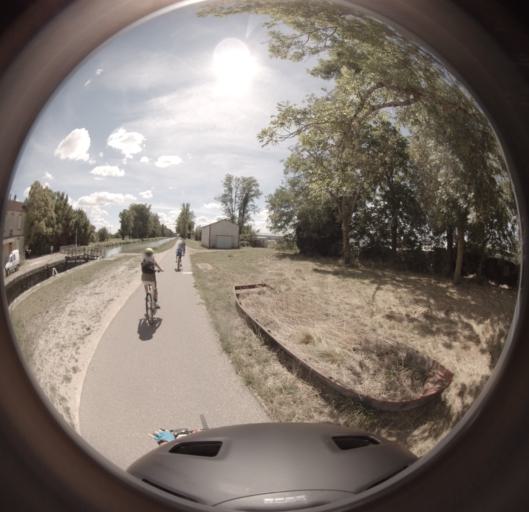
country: FR
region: Midi-Pyrenees
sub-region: Departement du Tarn-et-Garonne
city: Castelsarrasin
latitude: 44.0629
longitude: 1.1025
